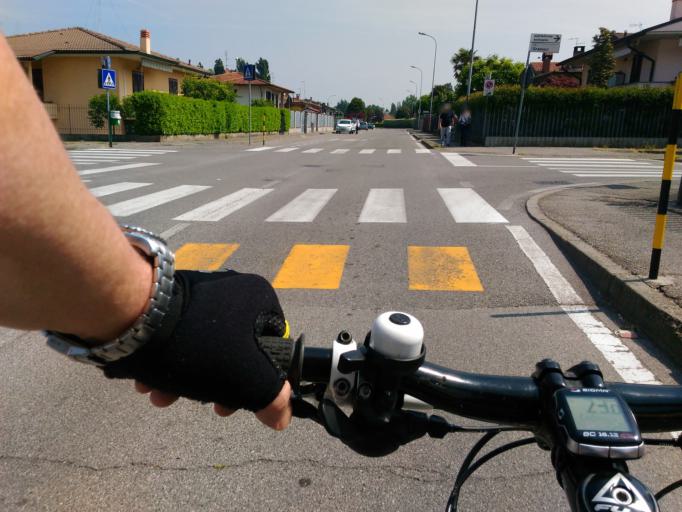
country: IT
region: Lombardy
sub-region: Provincia di Lodi
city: Muzza di Cornegliano Laudense
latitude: 45.2806
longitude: 9.4699
